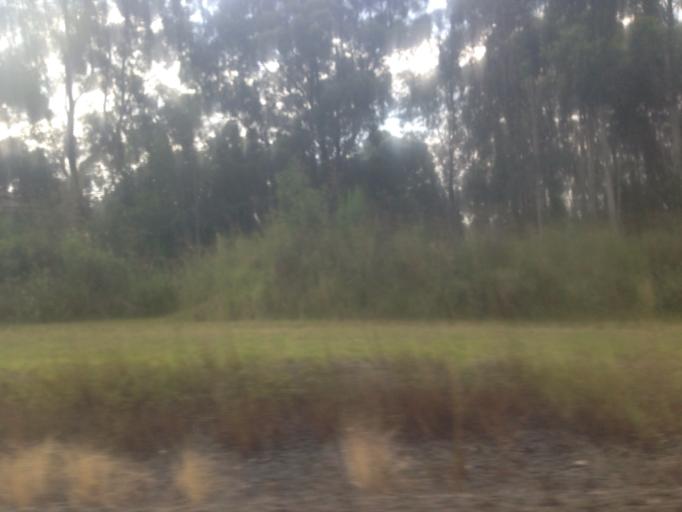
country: AU
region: New South Wales
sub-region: North Sydney
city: St Leonards
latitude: -33.8187
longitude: 151.1935
